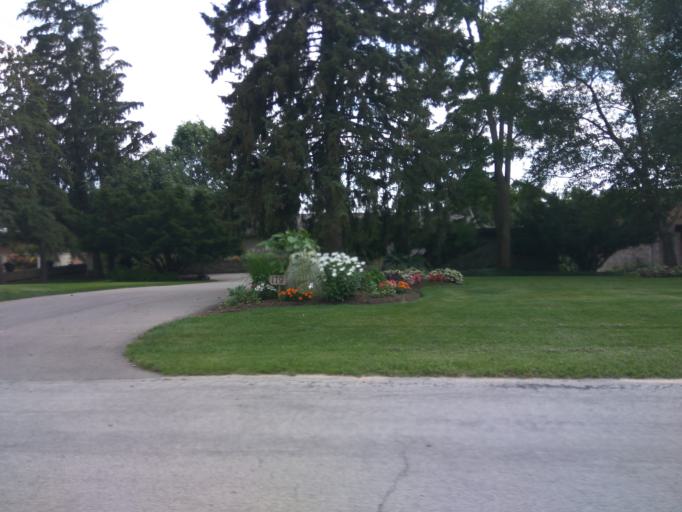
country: CA
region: Ontario
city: Cambridge
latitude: 43.4048
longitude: -80.3926
